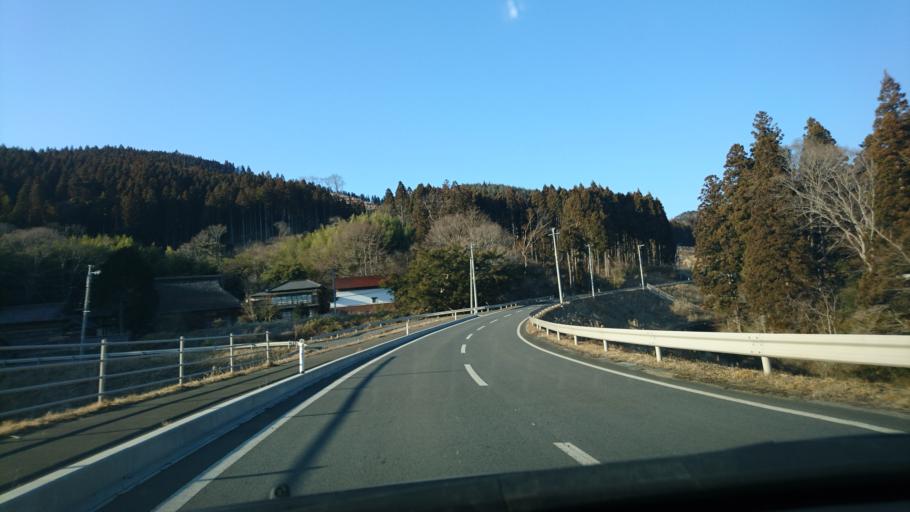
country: JP
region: Iwate
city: Ichinoseki
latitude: 38.8509
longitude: 141.3902
